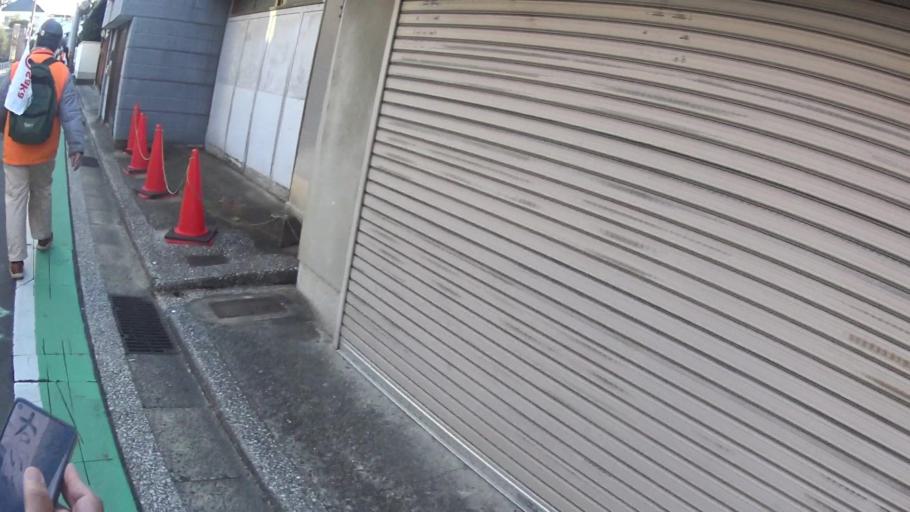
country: JP
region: Osaka
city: Kashihara
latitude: 34.5763
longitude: 135.5939
